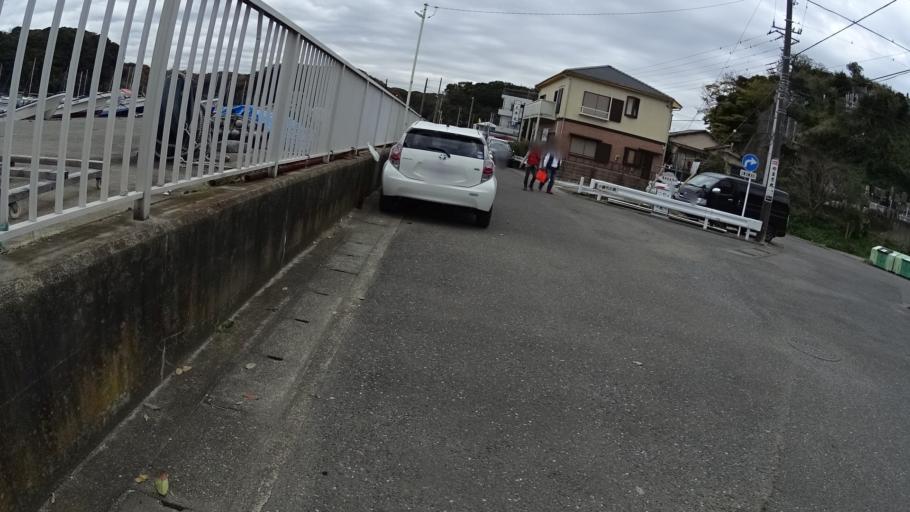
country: JP
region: Kanagawa
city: Miura
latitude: 35.1621
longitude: 139.6235
